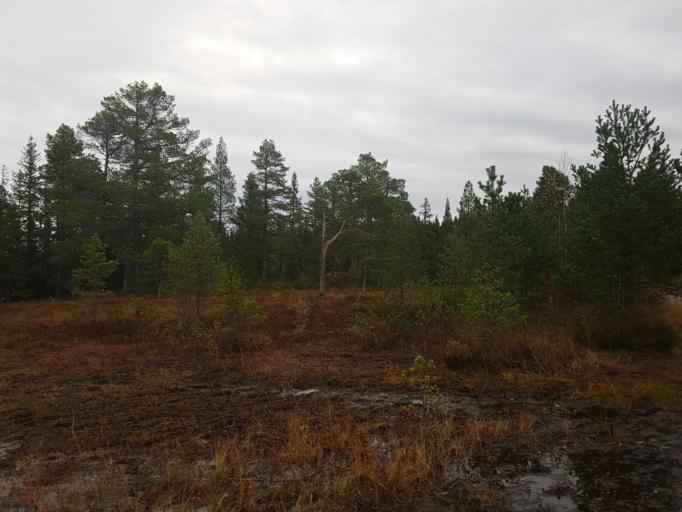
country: NO
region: Sor-Trondelag
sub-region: Melhus
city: Melhus
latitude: 63.3831
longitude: 10.2488
